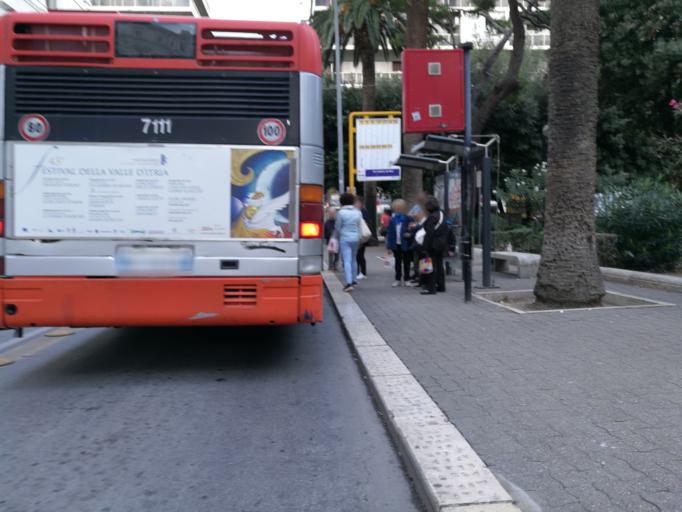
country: IT
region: Apulia
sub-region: Provincia di Bari
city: Bari
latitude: 41.1208
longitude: 16.8692
